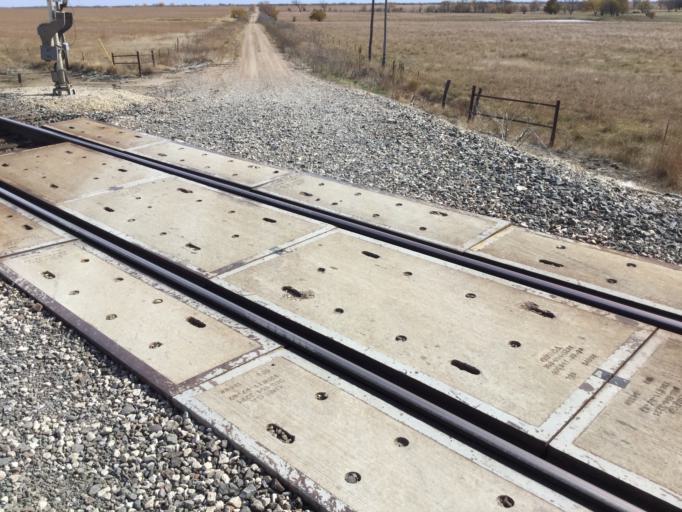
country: US
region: Kansas
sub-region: Butler County
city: El Dorado
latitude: 37.9704
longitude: -96.6991
